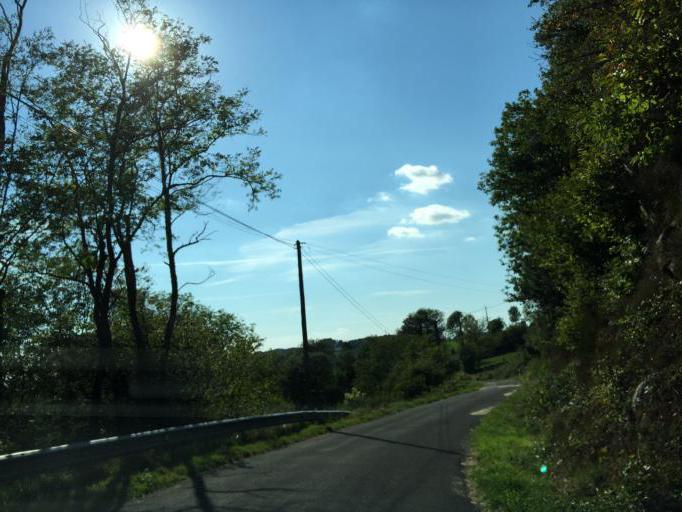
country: FR
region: Midi-Pyrenees
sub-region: Departement de l'Aveyron
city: Espalion
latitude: 44.5959
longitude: 2.6949
